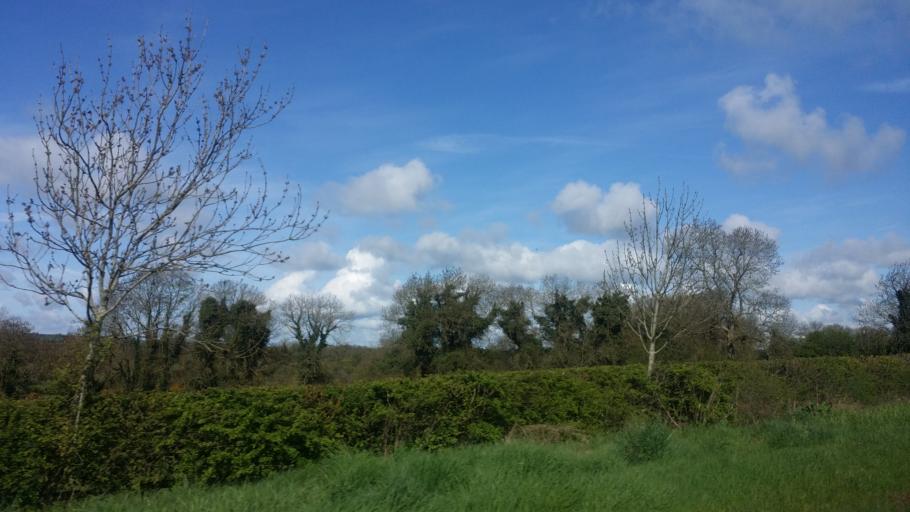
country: IE
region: Ulster
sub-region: An Cabhan
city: Mullagh
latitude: 53.7649
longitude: -6.9917
